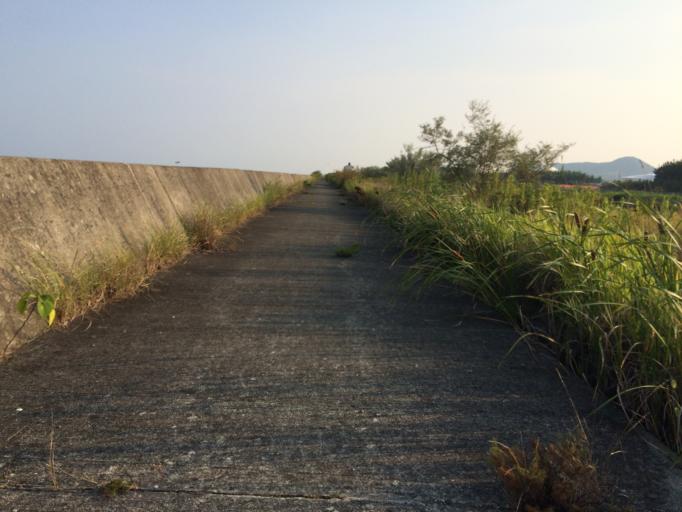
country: JP
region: Yamaguchi
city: Ogori-shimogo
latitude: 34.0150
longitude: 131.3807
